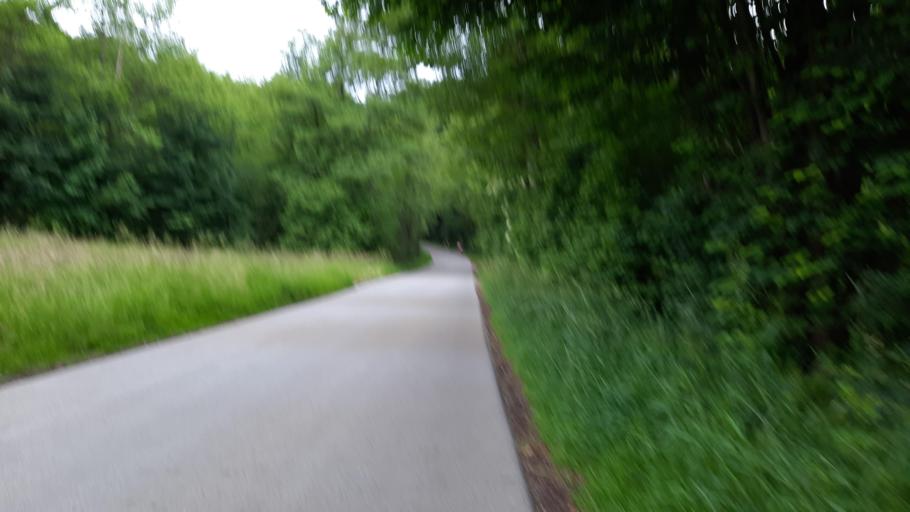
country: DE
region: Bavaria
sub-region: Upper Bavaria
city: Vagen
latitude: 47.8426
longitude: 11.8631
